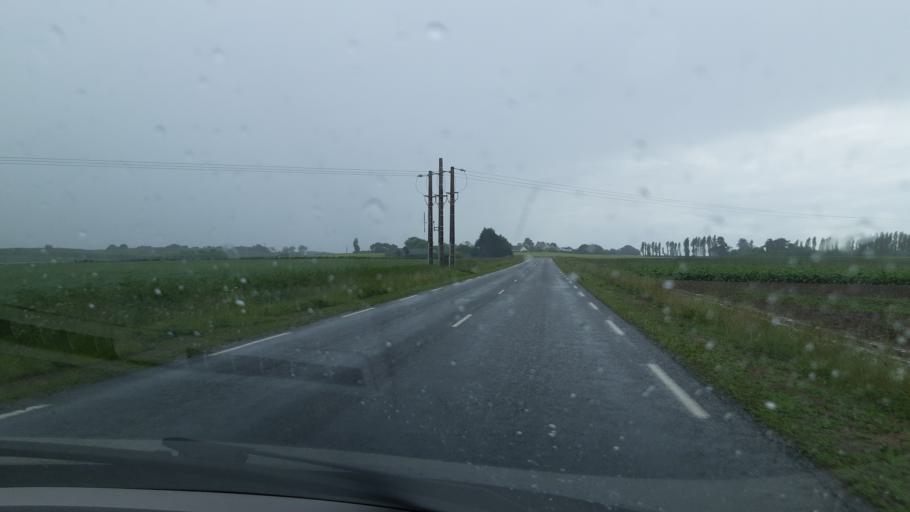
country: FR
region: Brittany
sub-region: Departement du Finistere
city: Plougoulm
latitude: 48.6282
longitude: -4.0553
